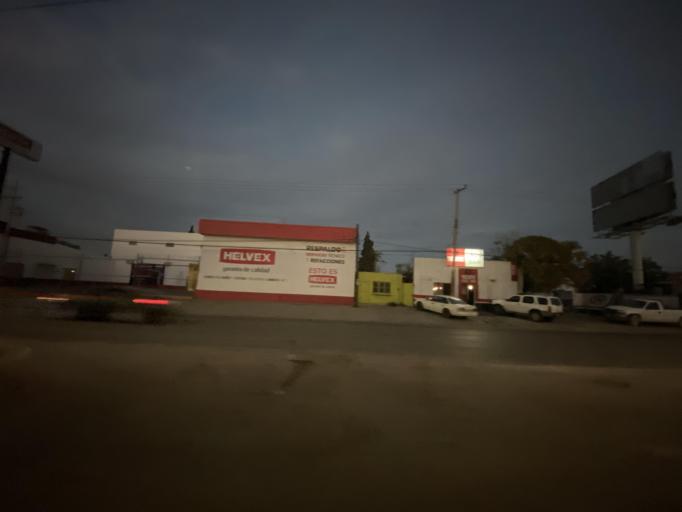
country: MX
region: Chihuahua
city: Ciudad Juarez
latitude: 31.7042
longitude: -106.4460
